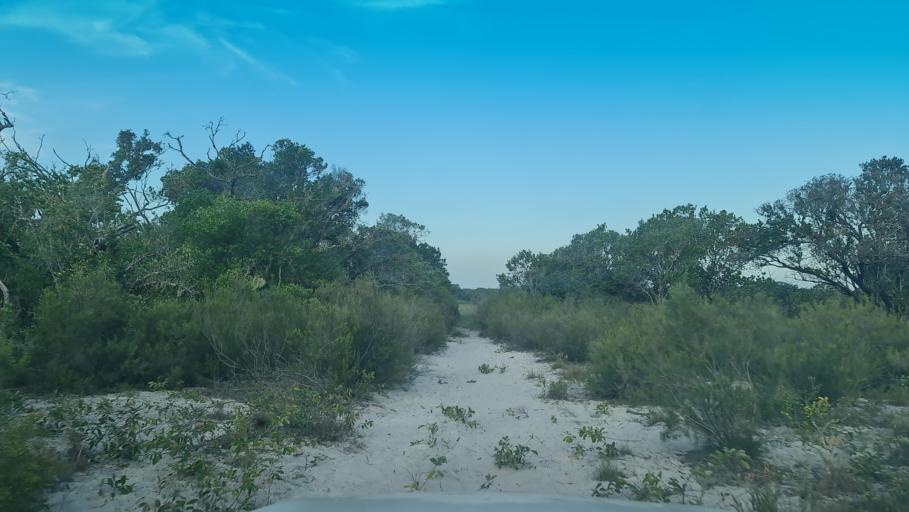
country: MZ
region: Gaza
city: Macia
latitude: -25.2146
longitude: 33.0527
